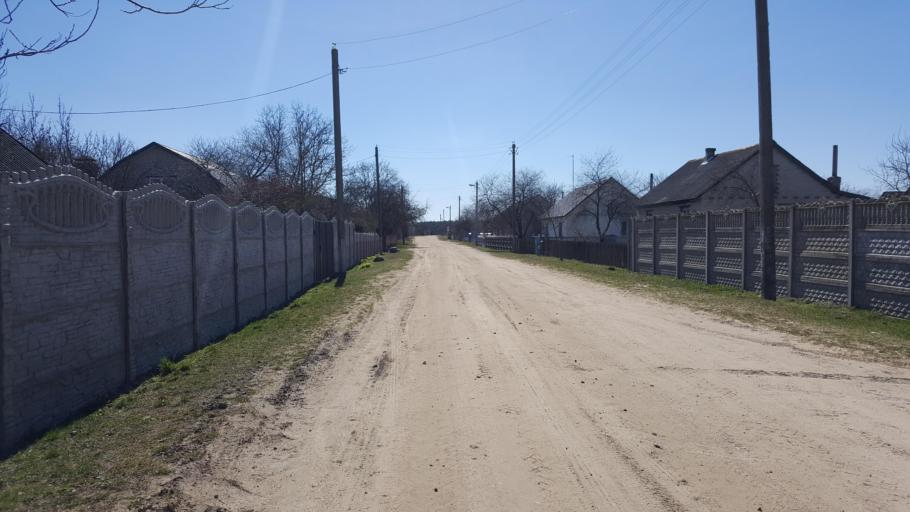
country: BY
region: Brest
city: Kamyanyets
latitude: 52.2930
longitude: 23.8565
